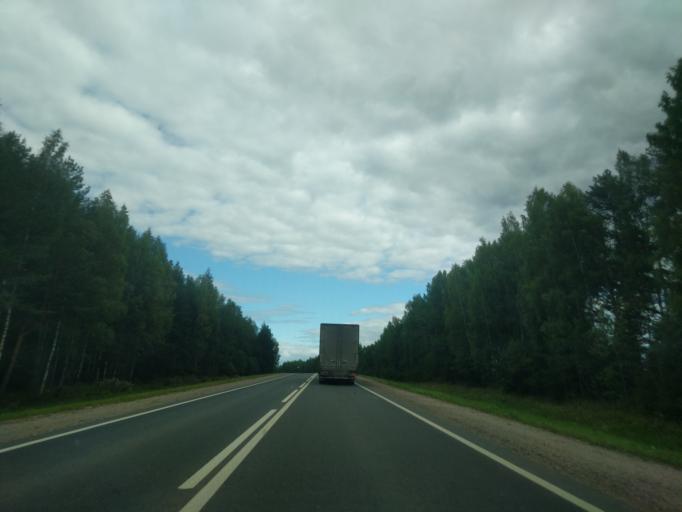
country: RU
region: Kostroma
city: Ostrovskoye
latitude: 57.8172
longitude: 42.2086
